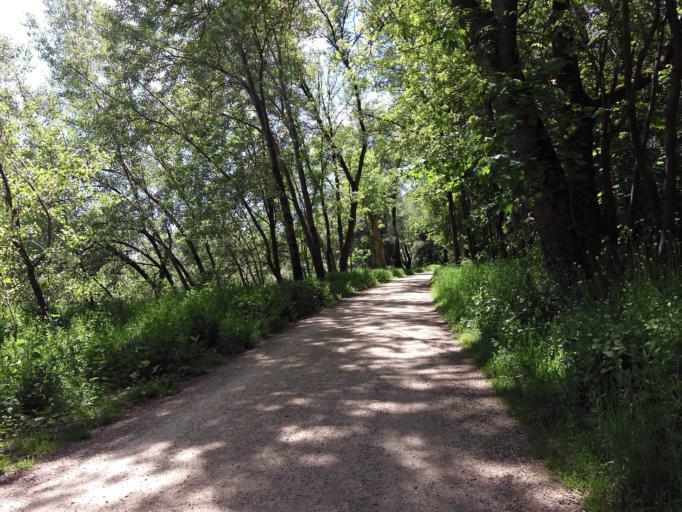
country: DE
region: Bavaria
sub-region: Upper Bavaria
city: Freising
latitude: 48.4012
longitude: 11.7591
